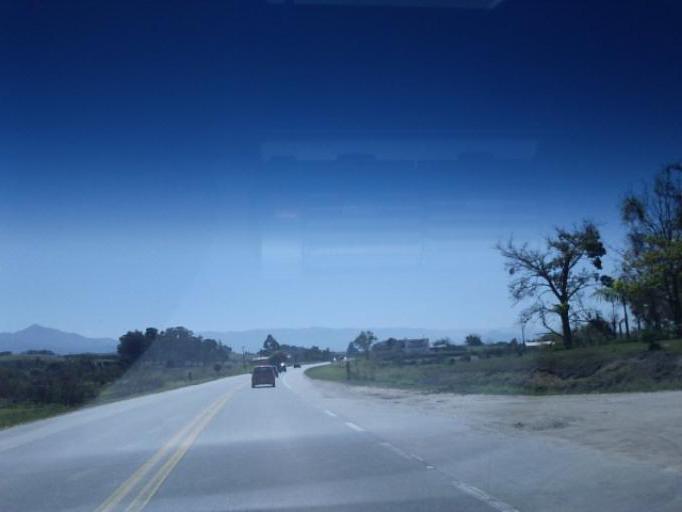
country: BR
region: Sao Paulo
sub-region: Tremembe
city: Tremembe
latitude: -22.9805
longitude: -45.6482
